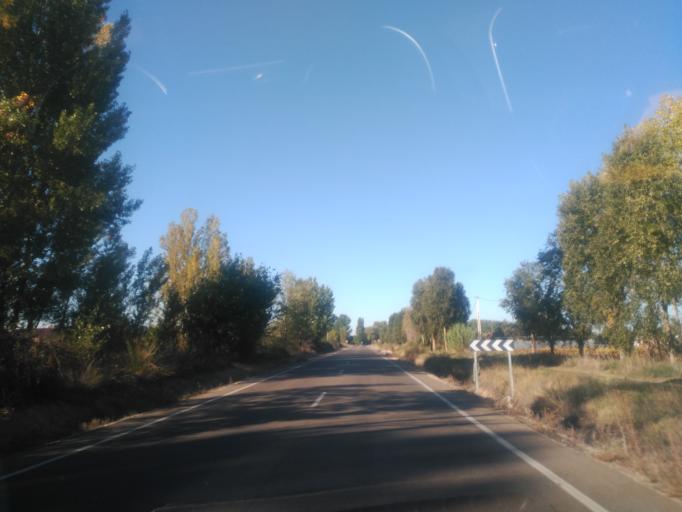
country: ES
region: Castille and Leon
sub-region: Provincia de Burgos
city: Fresnillo de las Duenas
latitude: 41.6791
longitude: -3.6414
